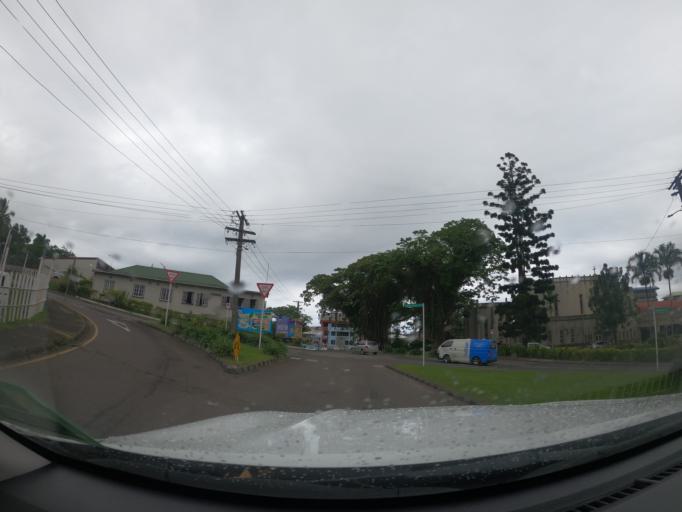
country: FJ
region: Central
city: Suva
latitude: -18.1419
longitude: 178.4249
